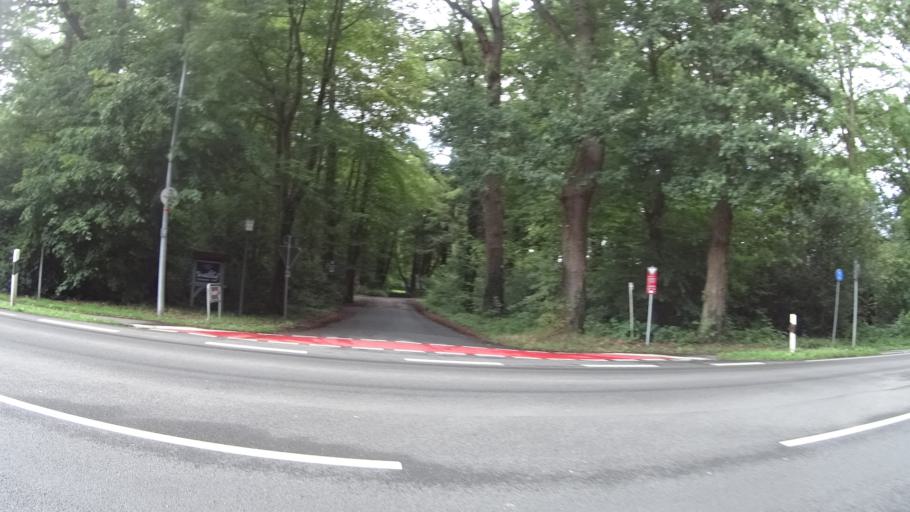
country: DE
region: Lower Saxony
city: Zetel
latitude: 53.3919
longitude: 7.9641
